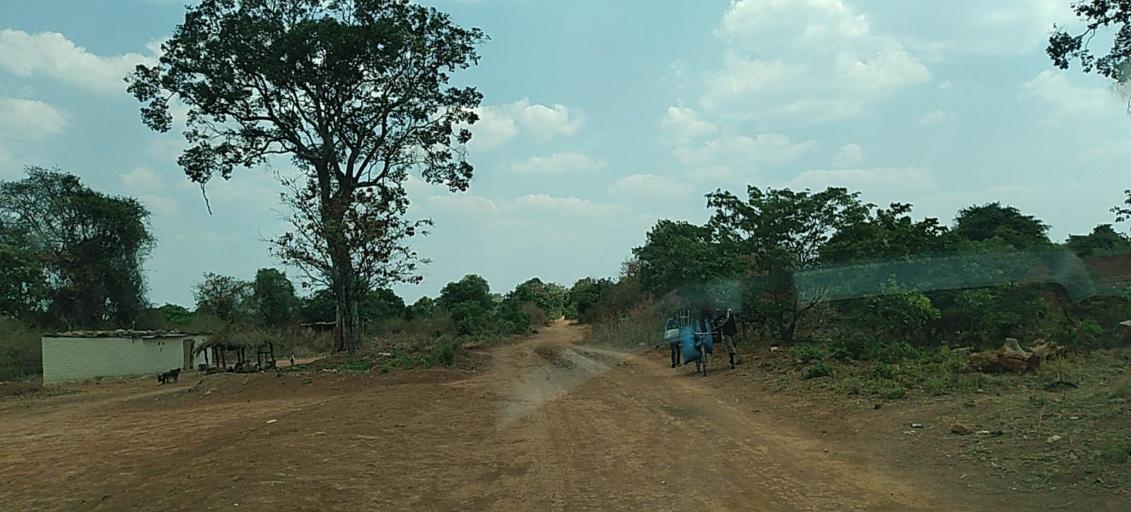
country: CD
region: Katanga
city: Kipushi
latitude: -12.0308
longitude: 27.4360
